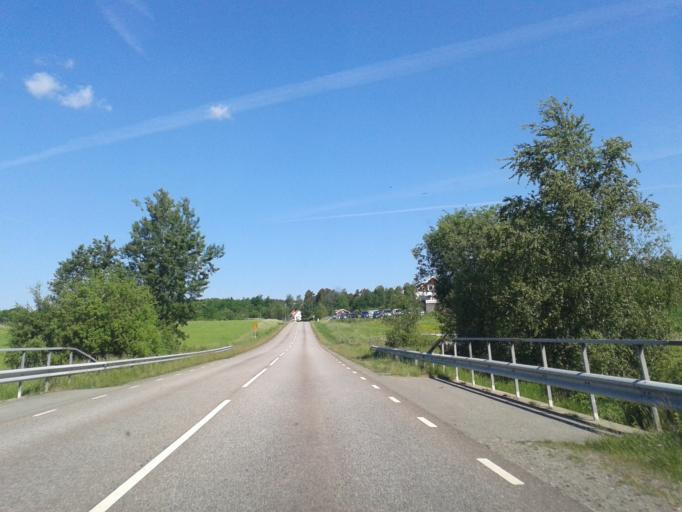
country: SE
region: Vaestra Goetaland
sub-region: Kungalvs Kommun
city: Kode
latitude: 57.9187
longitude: 11.9172
